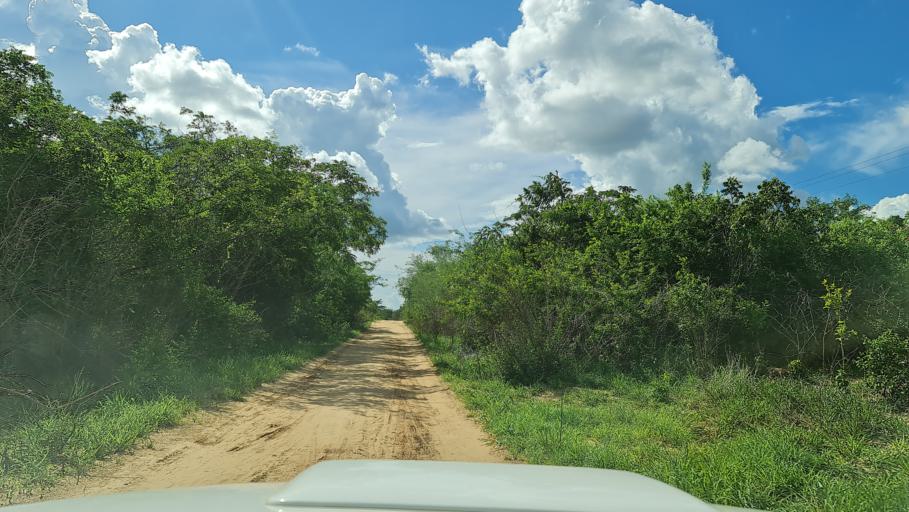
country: MZ
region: Nampula
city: Ilha de Mocambique
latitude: -15.4122
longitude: 40.2528
